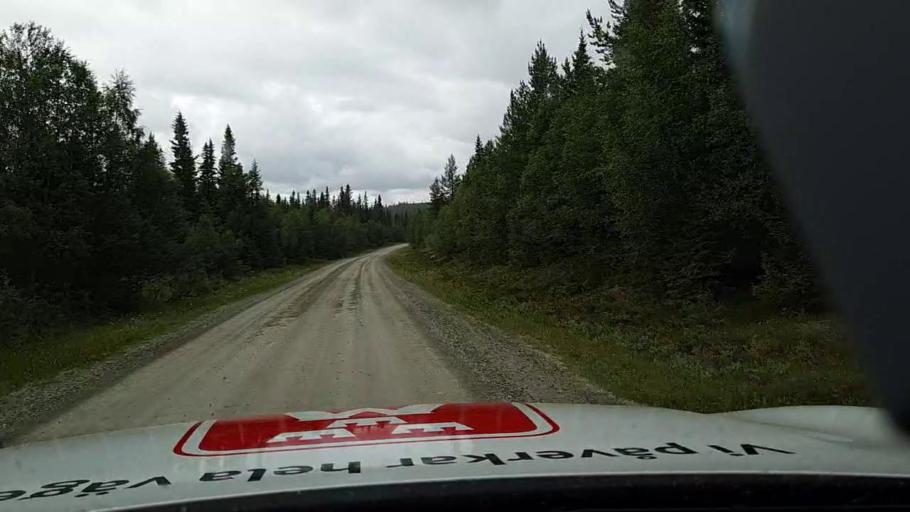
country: SE
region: Jaemtland
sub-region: Bergs Kommun
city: Hoverberg
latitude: 62.8434
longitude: 13.8383
